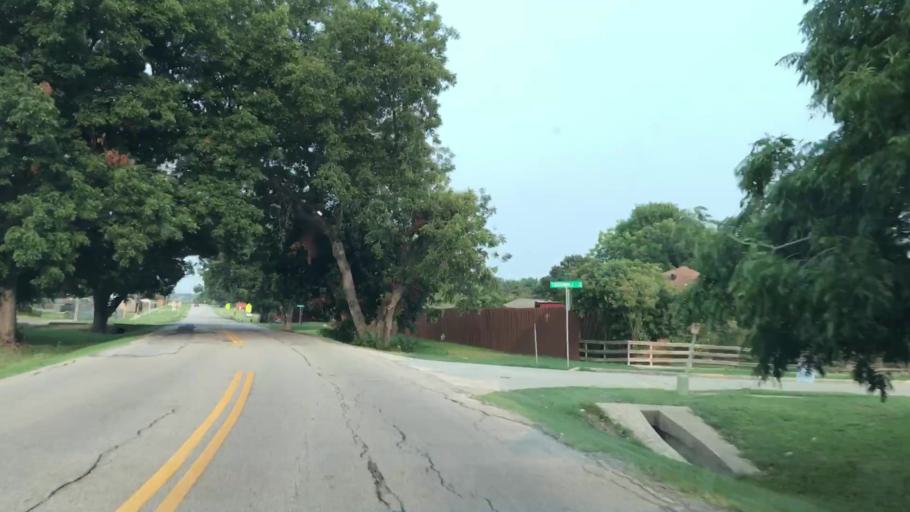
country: US
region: Texas
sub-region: Dallas County
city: Garland
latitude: 32.9193
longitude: -96.6050
